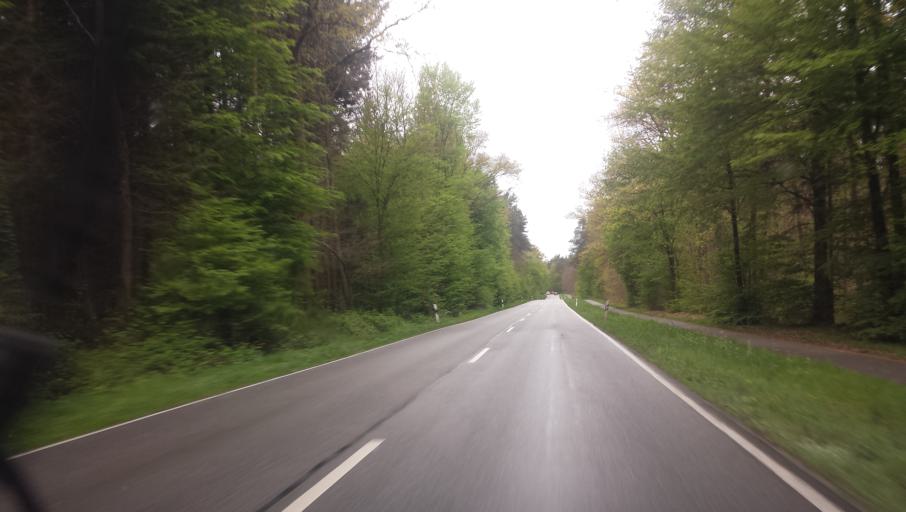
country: DE
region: Rheinland-Pfalz
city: Jockgrim
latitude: 49.0956
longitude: 8.2612
